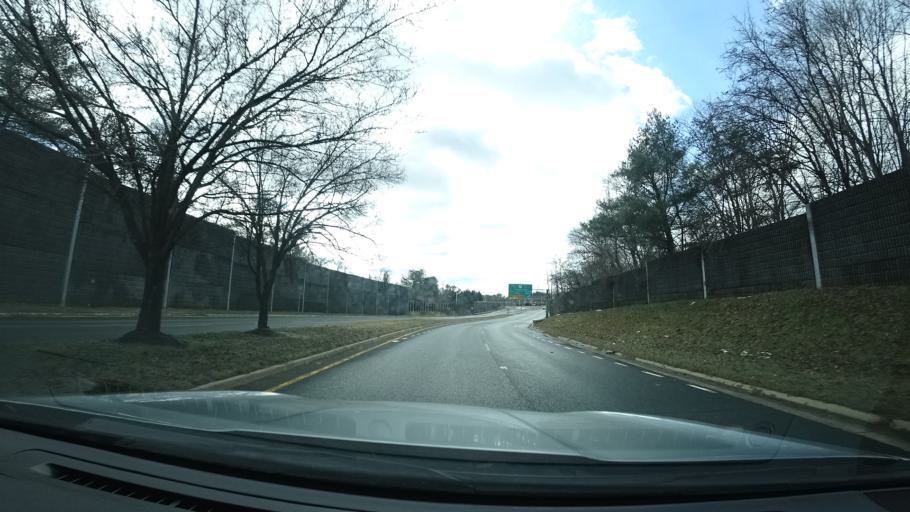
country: US
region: Virginia
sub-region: Fairfax County
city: Dranesville
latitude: 39.0142
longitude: -77.3626
